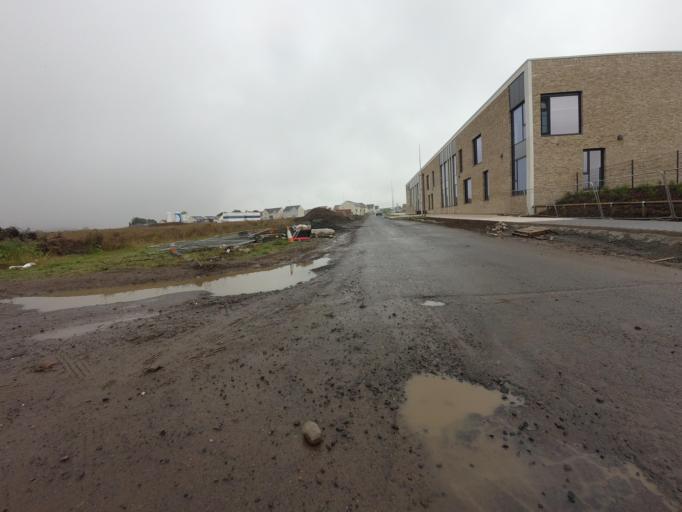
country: GB
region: Scotland
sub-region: West Lothian
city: East Calder
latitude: 55.9053
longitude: -3.4475
